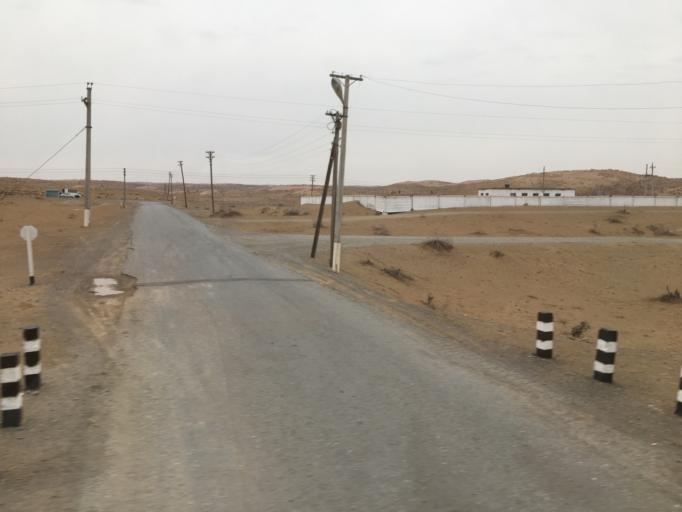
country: TM
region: Mary
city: Yoloeten
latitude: 36.4576
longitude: 62.5931
